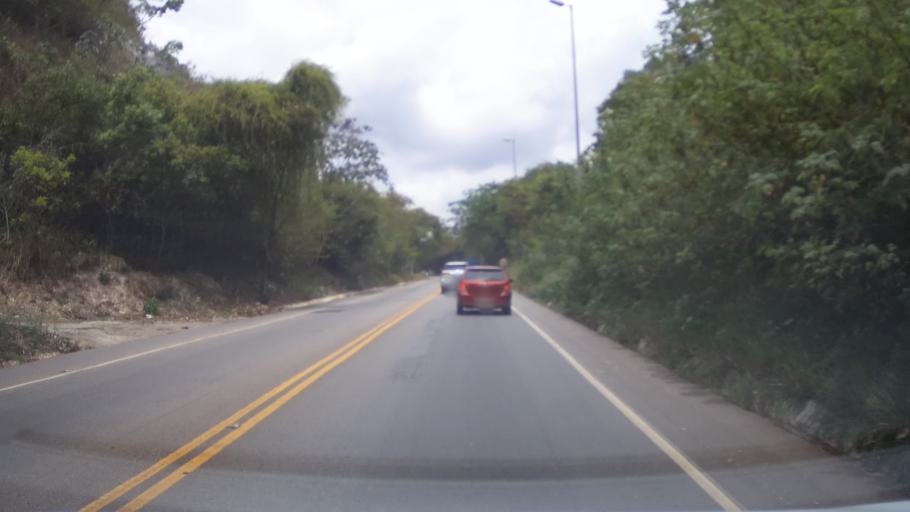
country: BR
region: Minas Gerais
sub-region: Nova Lima
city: Nova Lima
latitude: -19.9910
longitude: -43.8678
